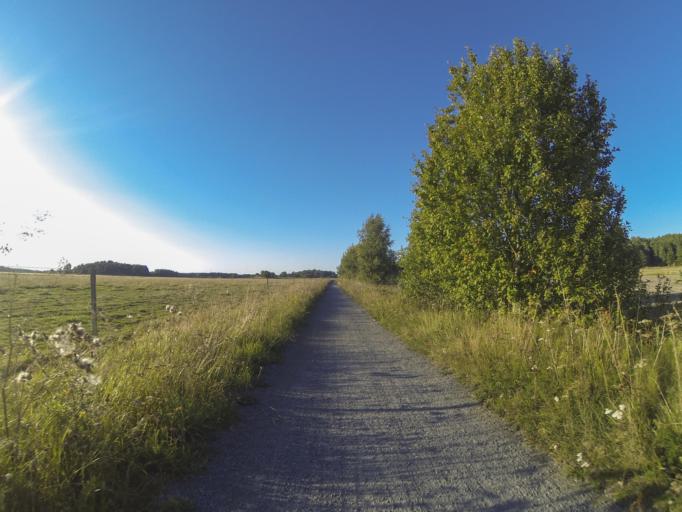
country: SE
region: Vaestmanland
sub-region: Vasteras
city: Vasteras
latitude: 59.5659
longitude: 16.6494
